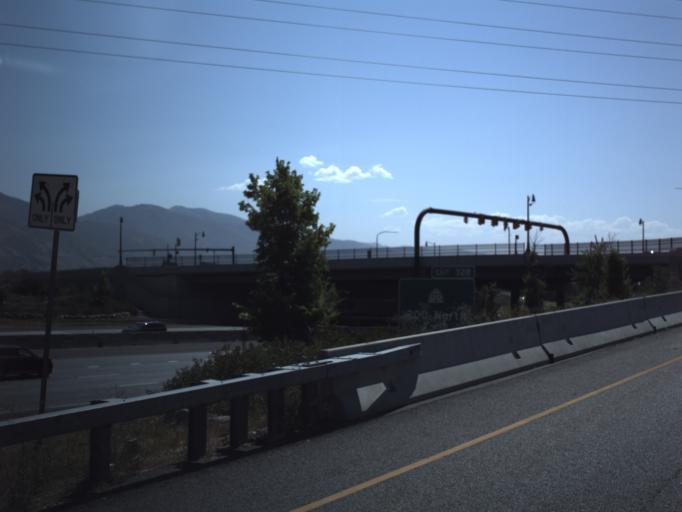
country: US
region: Utah
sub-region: Davis County
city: Layton
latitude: 41.0571
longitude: -111.9617
